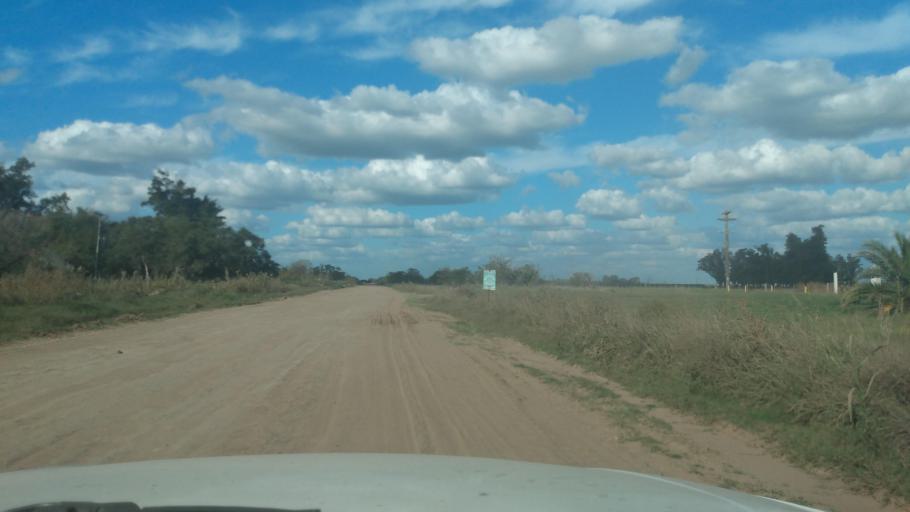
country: AR
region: Buenos Aires
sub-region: Partido de Navarro
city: Navarro
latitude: -35.0122
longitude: -59.4896
